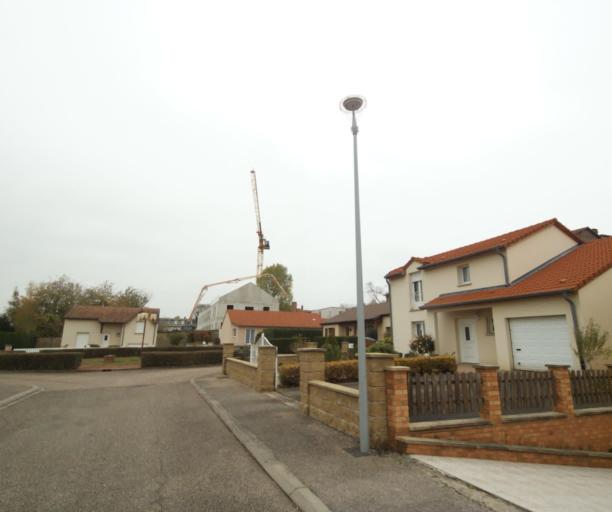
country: FR
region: Lorraine
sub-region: Departement de Meurthe-et-Moselle
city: Briey
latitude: 49.2450
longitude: 5.9314
